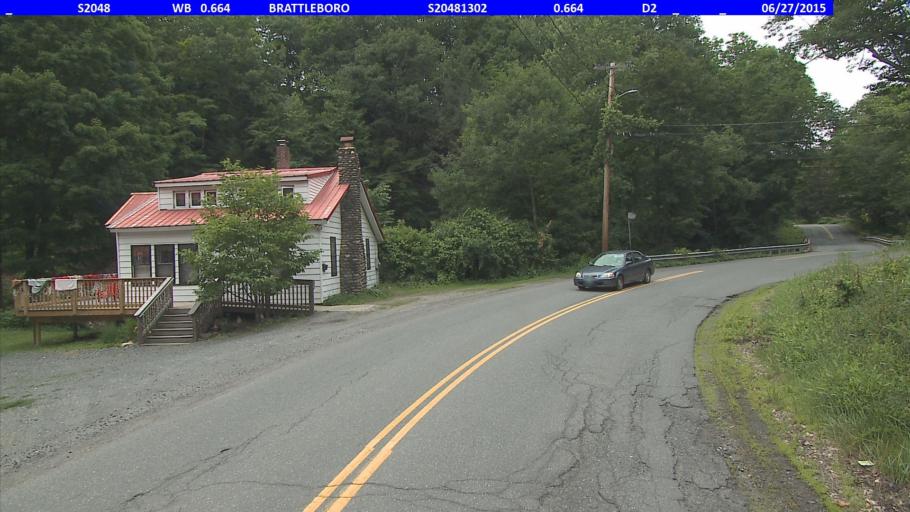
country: US
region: Vermont
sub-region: Windham County
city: Brattleboro
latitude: 42.8486
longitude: -72.5723
